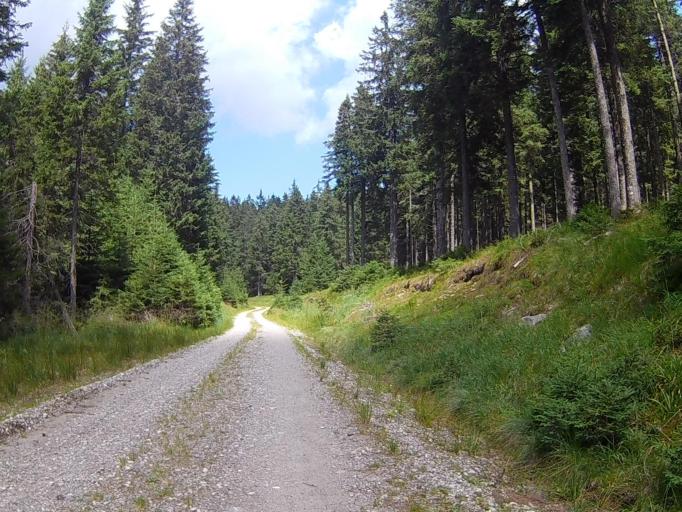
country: SI
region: Lovrenc na Pohorju
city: Lovrenc na Pohorju
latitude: 46.4813
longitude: 15.4019
